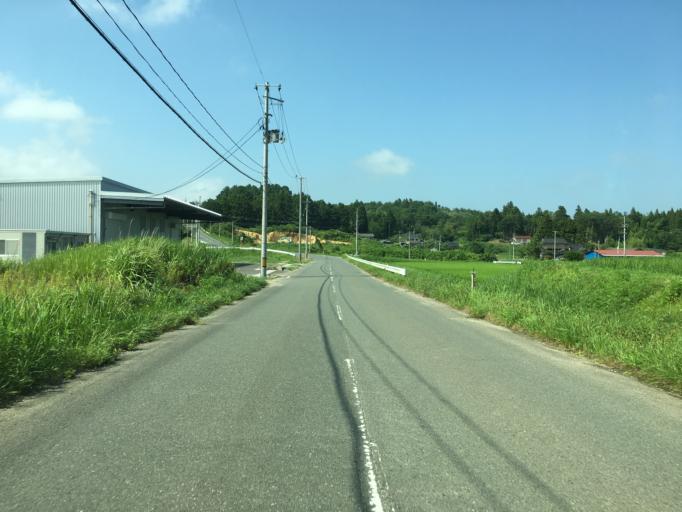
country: JP
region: Miyagi
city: Marumori
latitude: 37.8921
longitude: 140.8911
